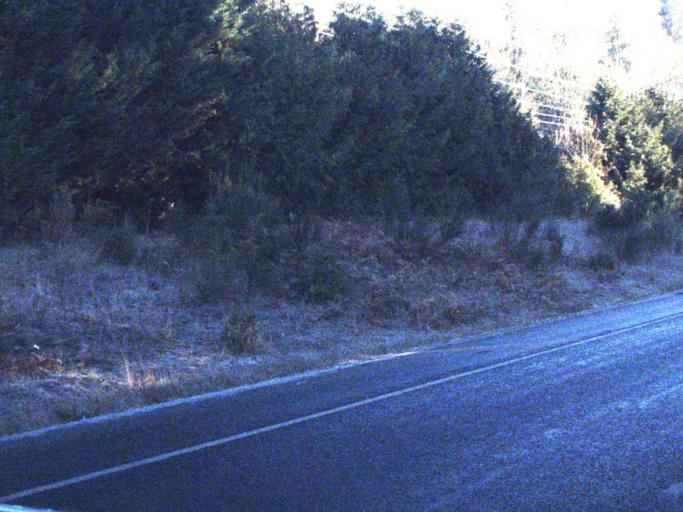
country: US
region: Washington
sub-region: Skagit County
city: Sedro-Woolley
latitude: 48.5276
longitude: -122.1016
